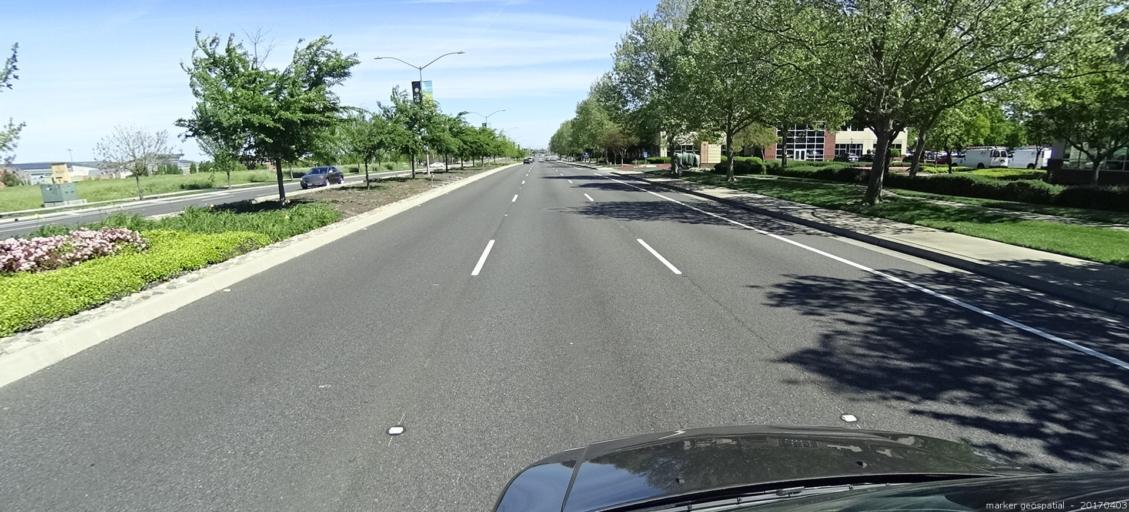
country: US
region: California
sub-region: Yolo County
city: West Sacramento
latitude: 38.6558
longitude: -121.5207
